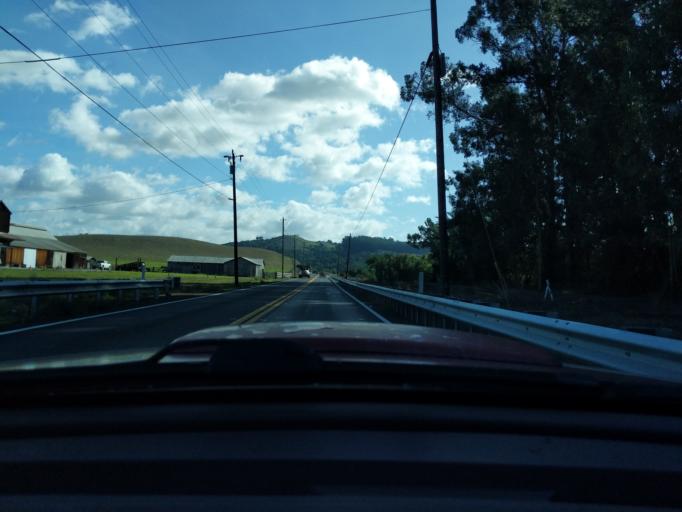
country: US
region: California
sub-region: San Benito County
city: Aromas
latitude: 36.9075
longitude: -121.6152
